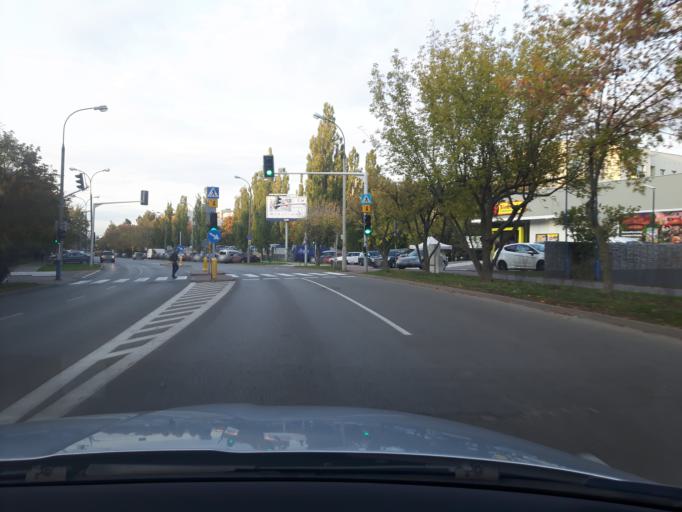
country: PL
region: Masovian Voivodeship
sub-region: Warszawa
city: Ursynow
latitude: 52.1581
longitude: 21.0373
